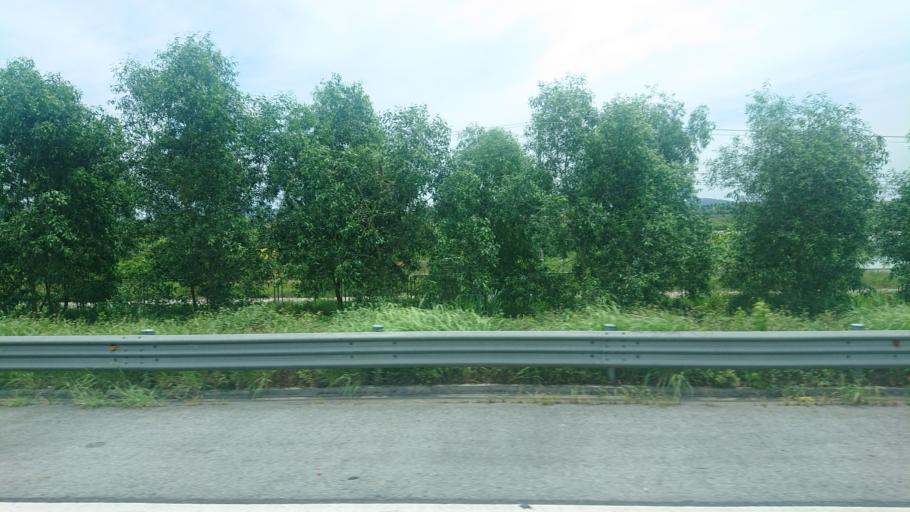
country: VN
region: Hai Phong
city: An Lao
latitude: 20.7888
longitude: 106.5559
